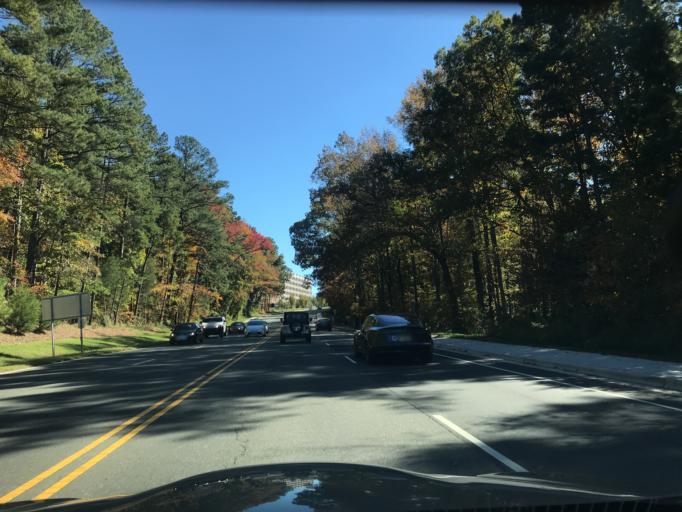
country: US
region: North Carolina
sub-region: Durham County
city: Durham
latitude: 35.9973
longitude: -78.9520
